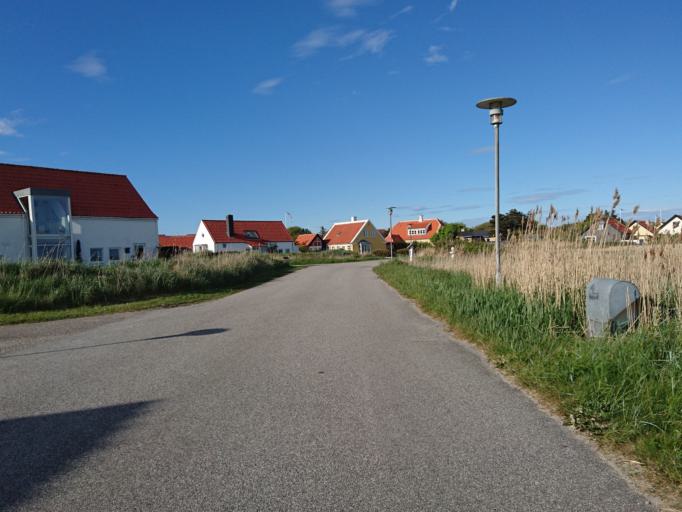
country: DK
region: North Denmark
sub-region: Frederikshavn Kommune
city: Skagen
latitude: 57.7144
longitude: 10.5662
